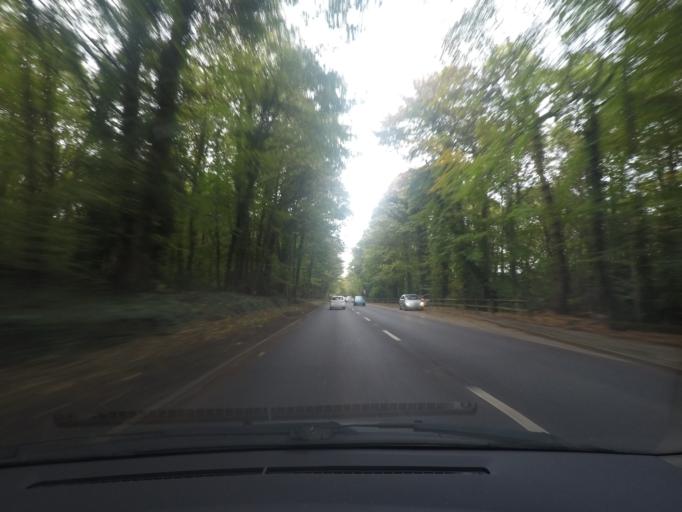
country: GB
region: England
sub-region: Sheffield
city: Chapletown
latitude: 53.4471
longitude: -1.4950
